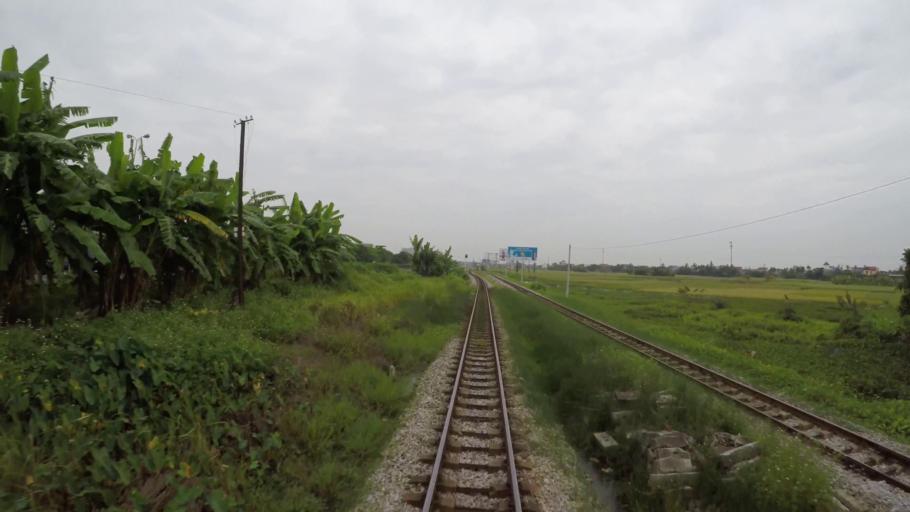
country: VN
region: Hai Duong
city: Phu Thai
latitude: 20.9318
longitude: 106.5529
